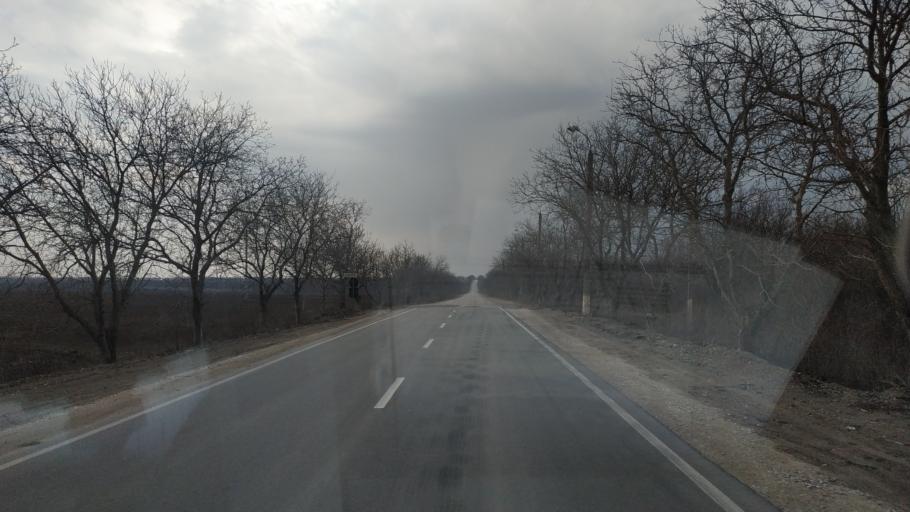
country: MD
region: Telenesti
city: Grigoriopol
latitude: 47.0196
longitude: 29.2900
